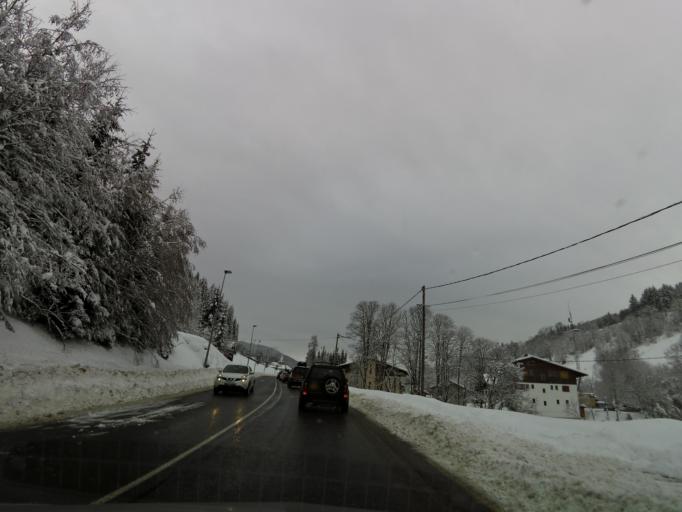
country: FR
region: Rhone-Alpes
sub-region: Departement de la Haute-Savoie
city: Les Gets
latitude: 46.1656
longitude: 6.6755
